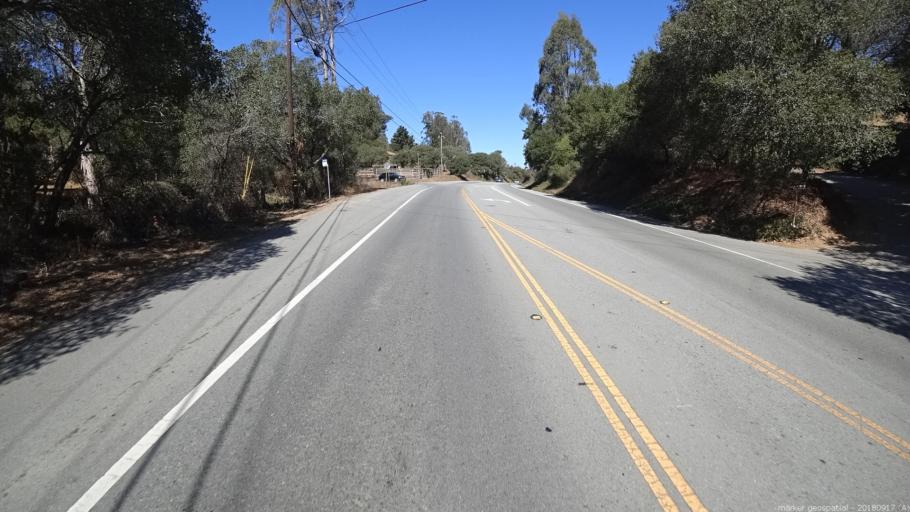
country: US
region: California
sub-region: Monterey County
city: Prunedale
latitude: 36.8298
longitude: -121.6785
